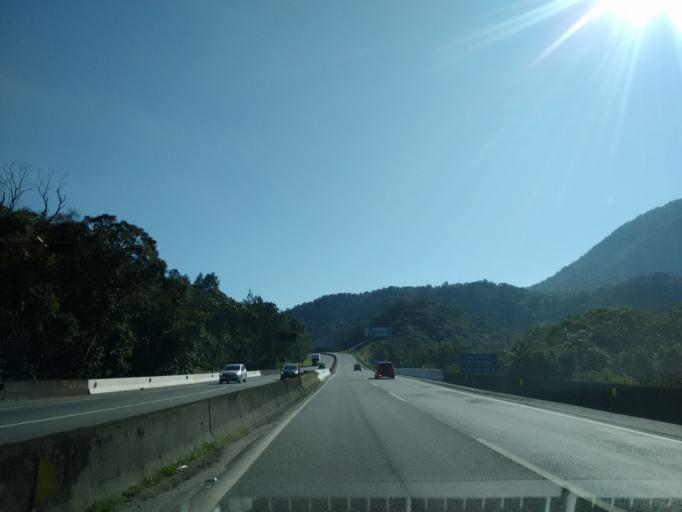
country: BR
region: Parana
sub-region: Guaratuba
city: Guaratuba
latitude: -25.9585
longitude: -48.9009
